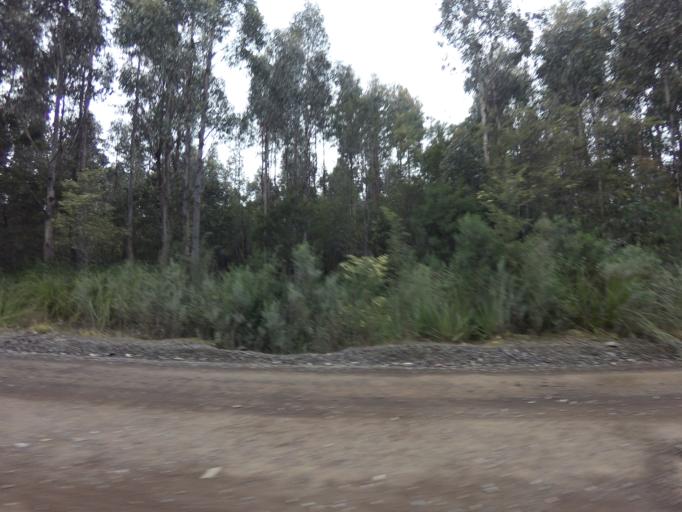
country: AU
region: Tasmania
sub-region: Huon Valley
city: Geeveston
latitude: -43.4717
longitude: 146.8921
